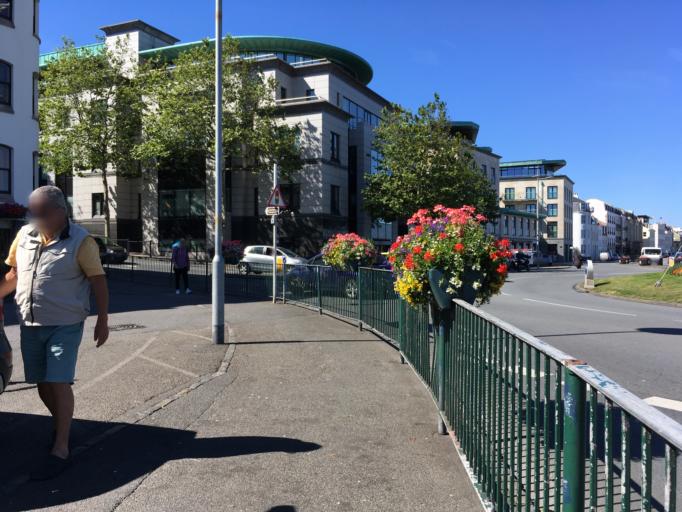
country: GG
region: St Peter Port
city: Saint Peter Port
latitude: 49.4586
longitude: -2.5347
